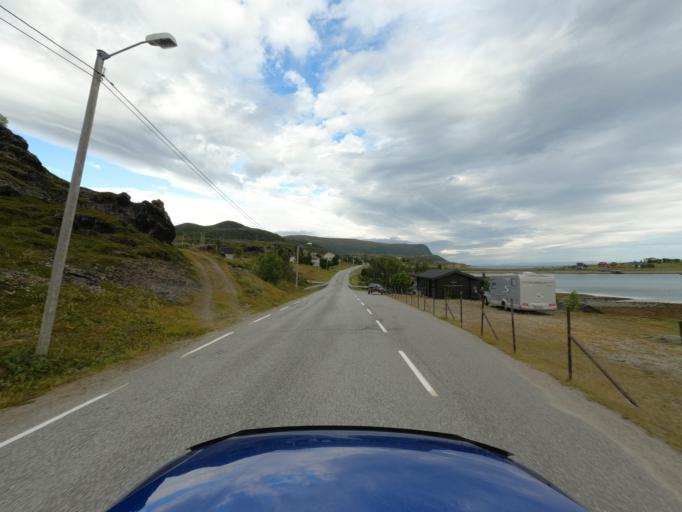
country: NO
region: Finnmark Fylke
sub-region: Porsanger
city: Lakselv
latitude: 70.5231
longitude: 25.0810
